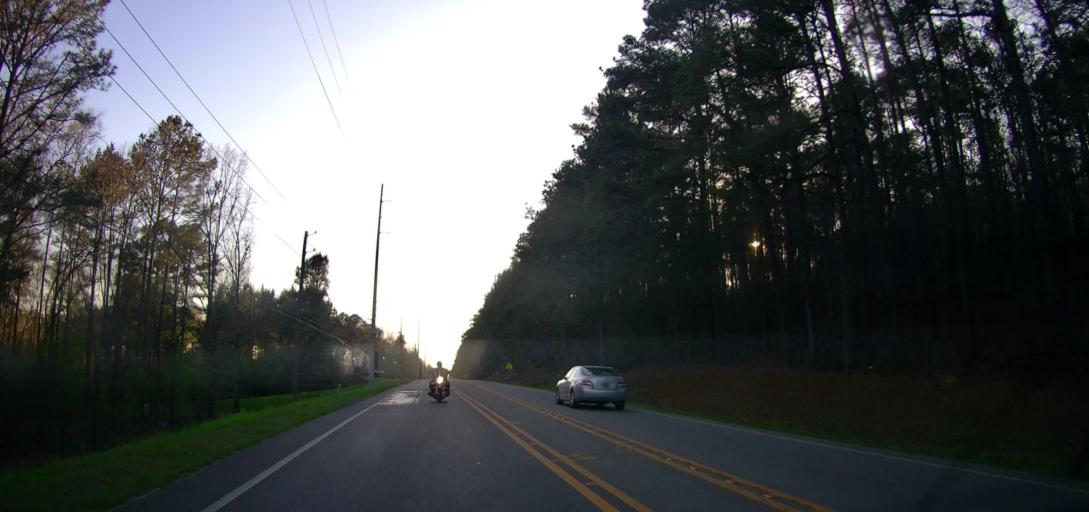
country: US
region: Alabama
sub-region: Shelby County
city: Chelsea
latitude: 33.3389
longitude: -86.6763
